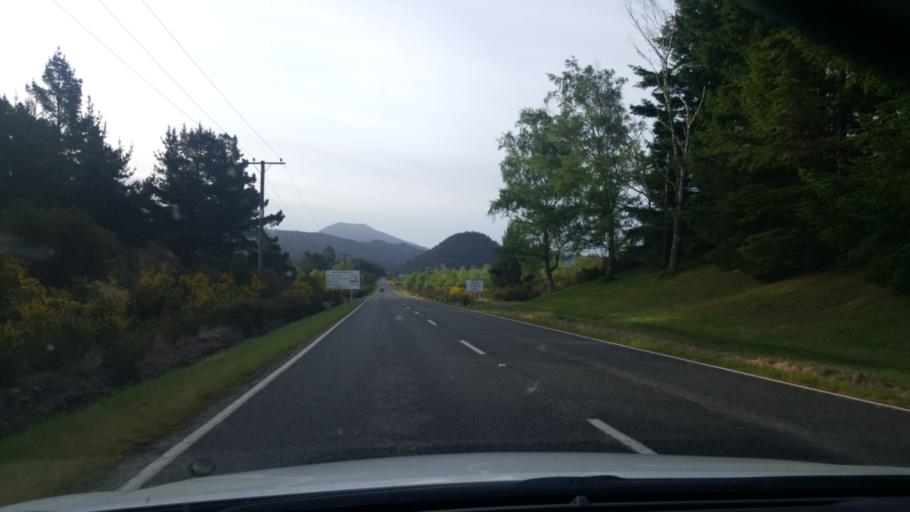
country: NZ
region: Waikato
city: Turangi
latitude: -38.9896
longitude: 175.7922
